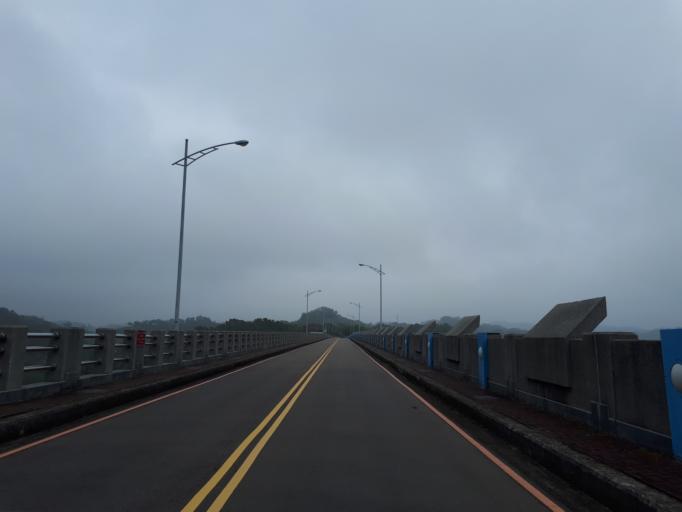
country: TW
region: Taiwan
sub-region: Hsinchu
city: Hsinchu
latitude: 24.7195
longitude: 121.0426
